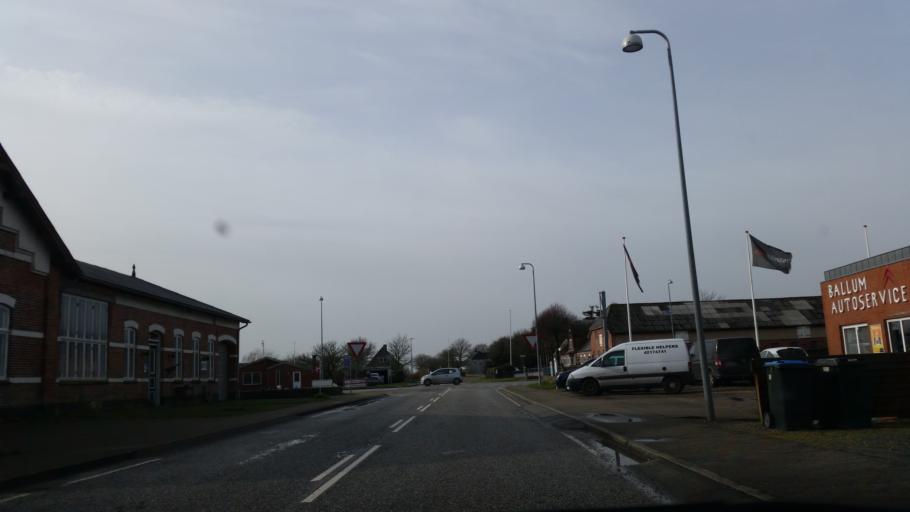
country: DK
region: South Denmark
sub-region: Tonder Kommune
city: Sherrebek
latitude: 55.0760
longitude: 8.6592
